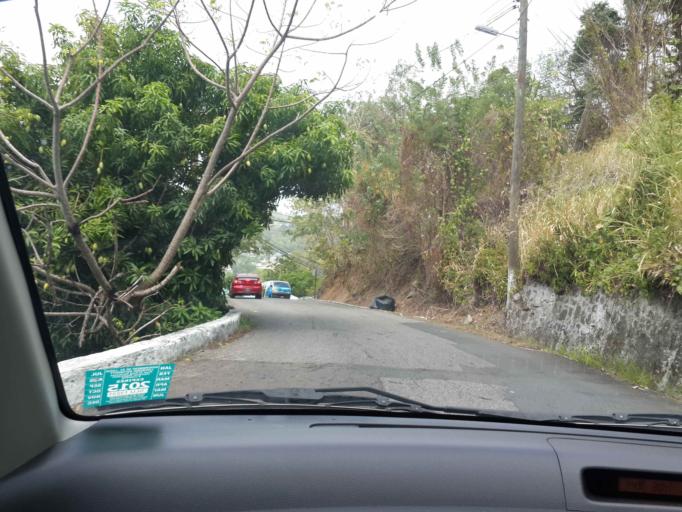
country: LC
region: Castries Quarter
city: Castries
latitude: 14.0065
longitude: -60.9951
